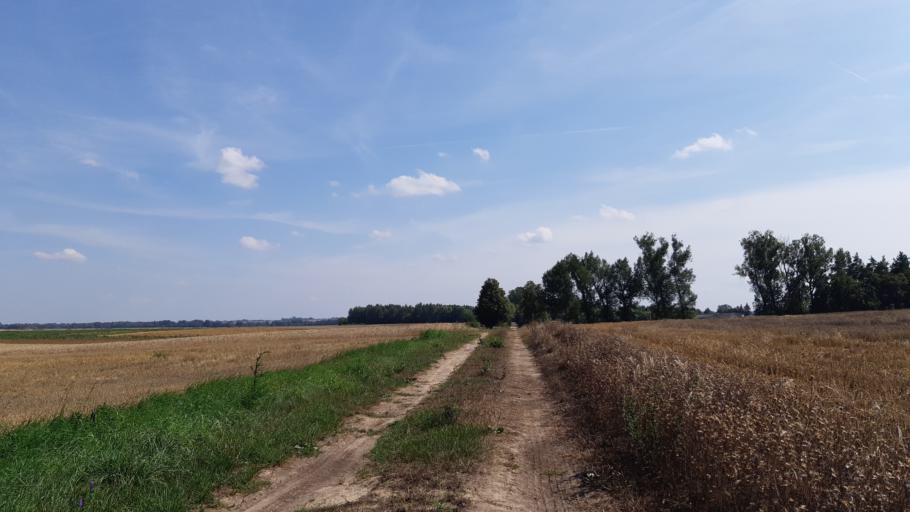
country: LT
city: Virbalis
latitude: 54.6415
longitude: 22.8197
